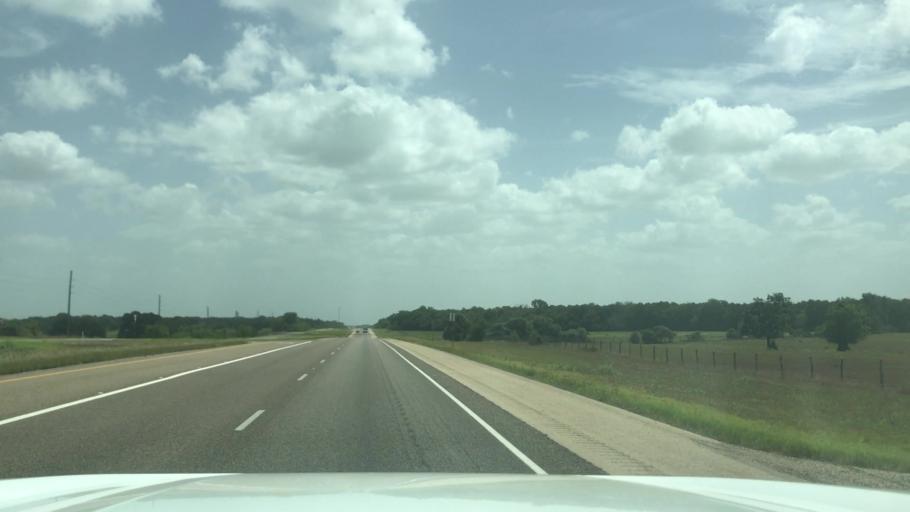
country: US
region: Texas
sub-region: Robertson County
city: Calvert
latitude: 31.0549
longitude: -96.7116
